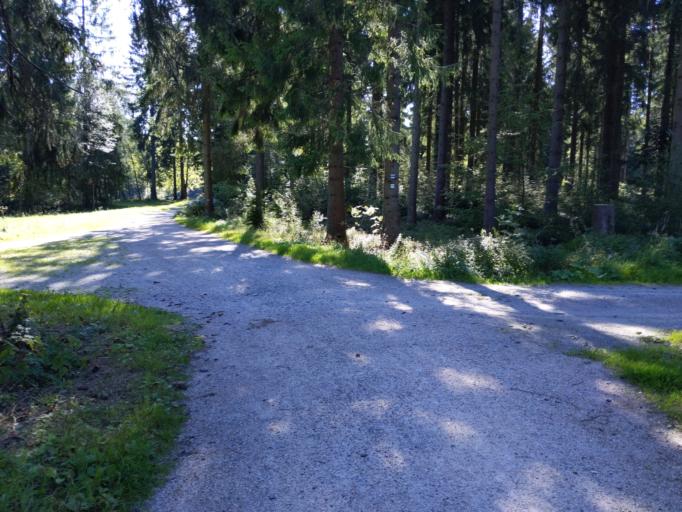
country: DE
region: Saxony
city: Pohl
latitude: 50.3943
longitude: 12.3515
